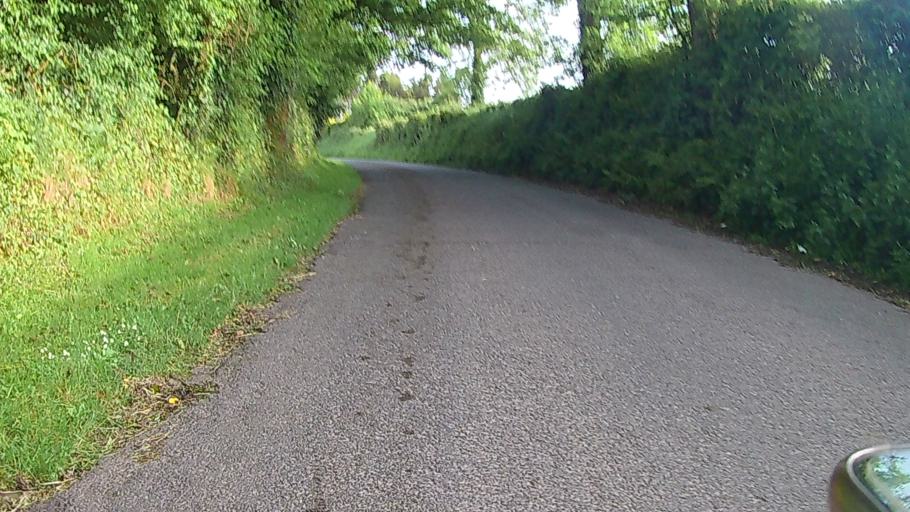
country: IE
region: Munster
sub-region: County Cork
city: Cork
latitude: 51.9864
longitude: -8.4583
